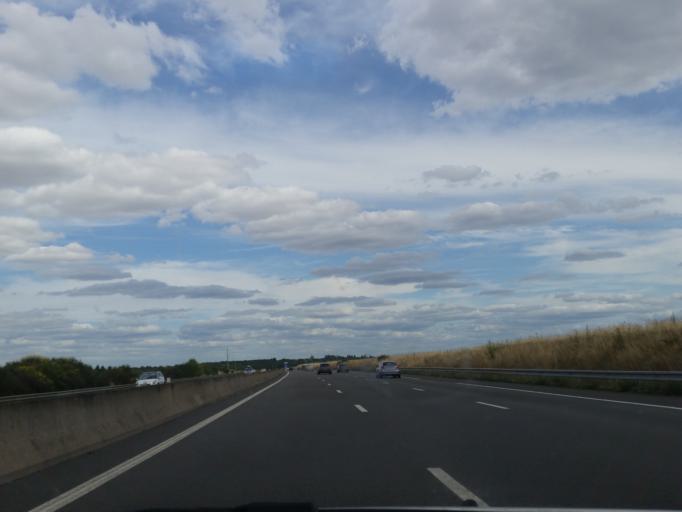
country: FR
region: Centre
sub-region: Departement du Loir-et-Cher
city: Herbault
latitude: 47.6162
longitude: 1.2010
